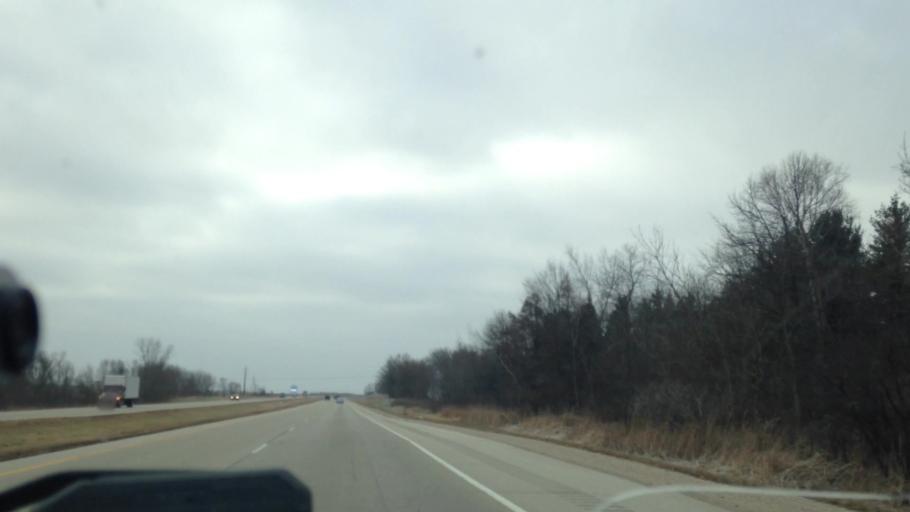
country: US
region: Wisconsin
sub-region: Washington County
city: Jackson
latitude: 43.3678
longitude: -88.1938
